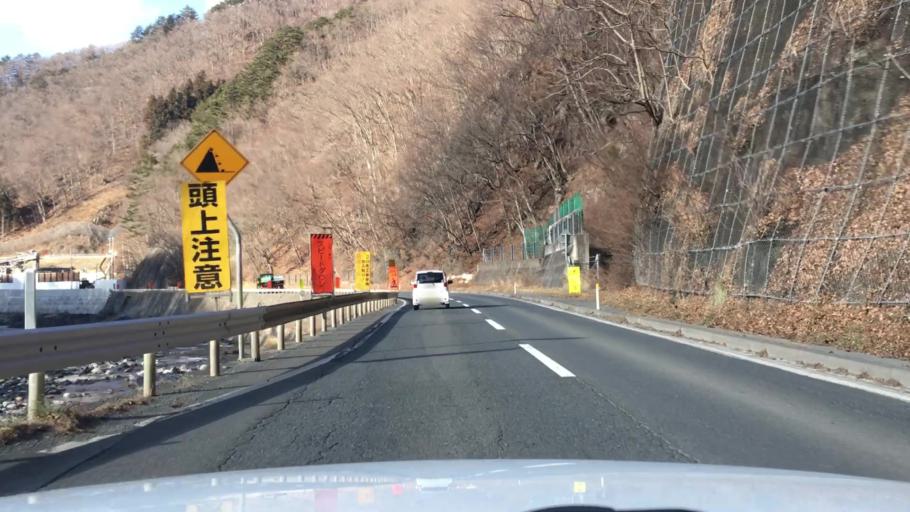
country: JP
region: Iwate
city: Miyako
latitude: 39.5997
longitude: 141.7132
